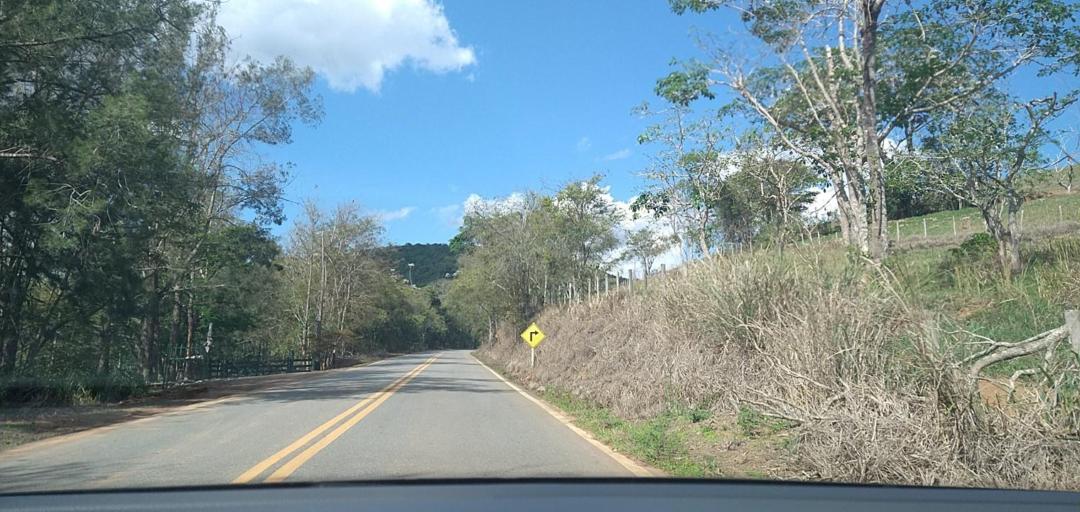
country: BR
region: Minas Gerais
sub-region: Alvinopolis
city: Alvinopolis
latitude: -20.0160
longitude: -43.0875
